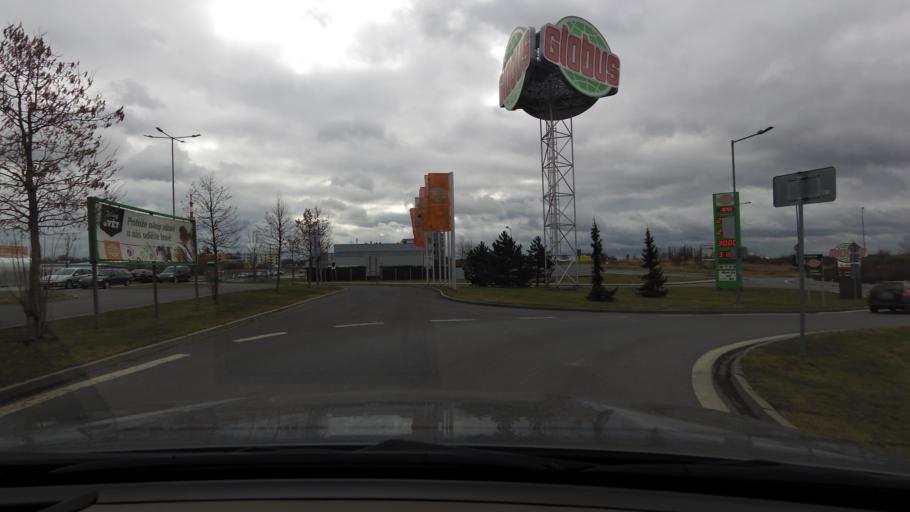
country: CZ
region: Plzensky
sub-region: Okres Plzen-Mesto
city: Pilsen
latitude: 49.7764
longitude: 13.3473
